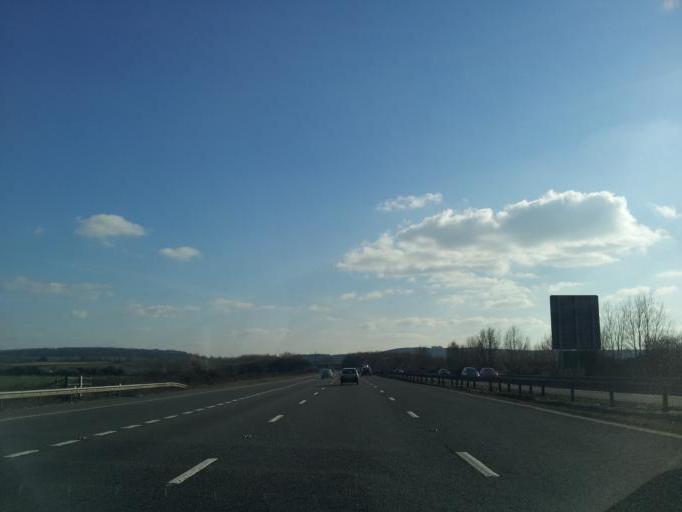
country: GB
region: England
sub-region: North Somerset
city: St. Georges
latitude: 51.3551
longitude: -2.8943
